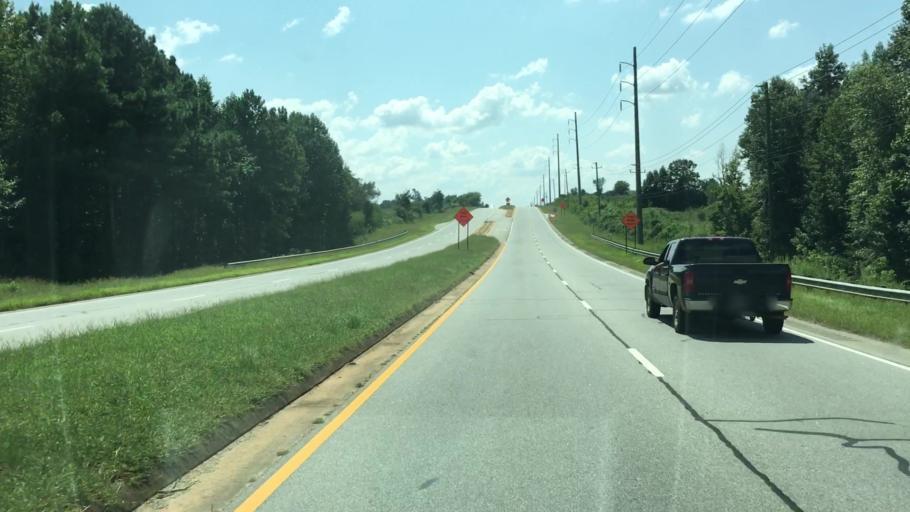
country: US
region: Georgia
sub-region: Morgan County
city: Madison
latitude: 33.5708
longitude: -83.4649
